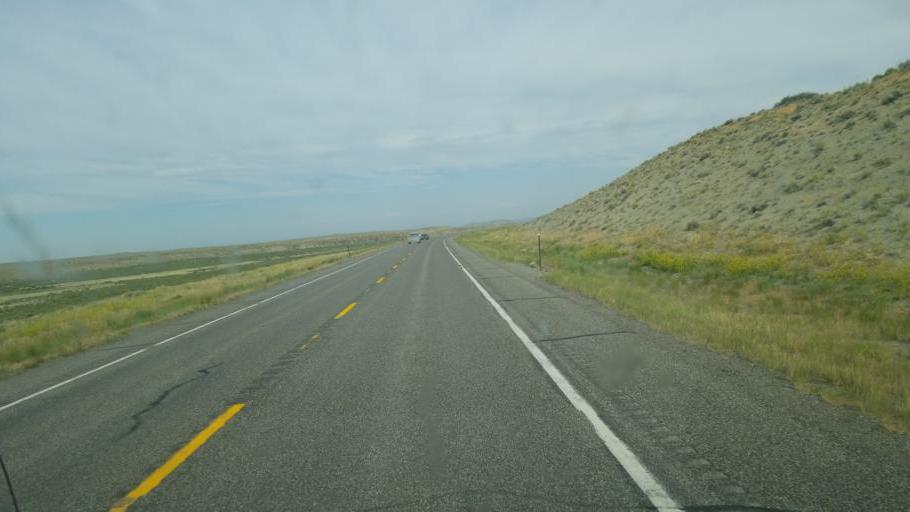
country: US
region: Wyoming
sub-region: Fremont County
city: Riverton
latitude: 43.2234
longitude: -108.0386
